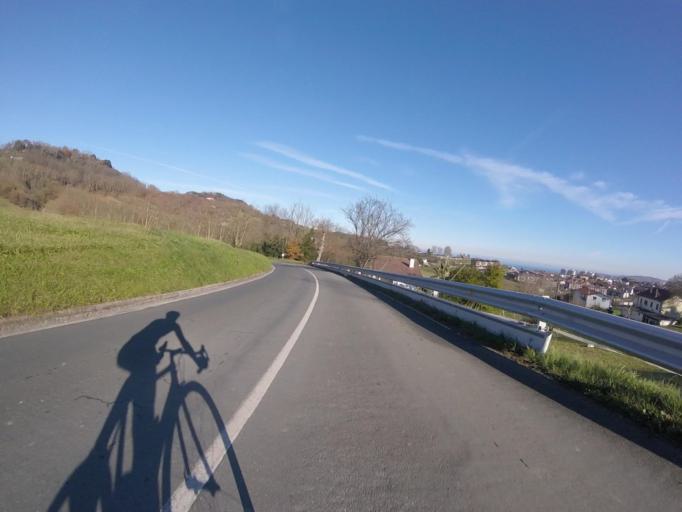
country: ES
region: Basque Country
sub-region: Provincia de Guipuzcoa
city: Fuenterrabia
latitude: 43.3647
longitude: -1.8069
